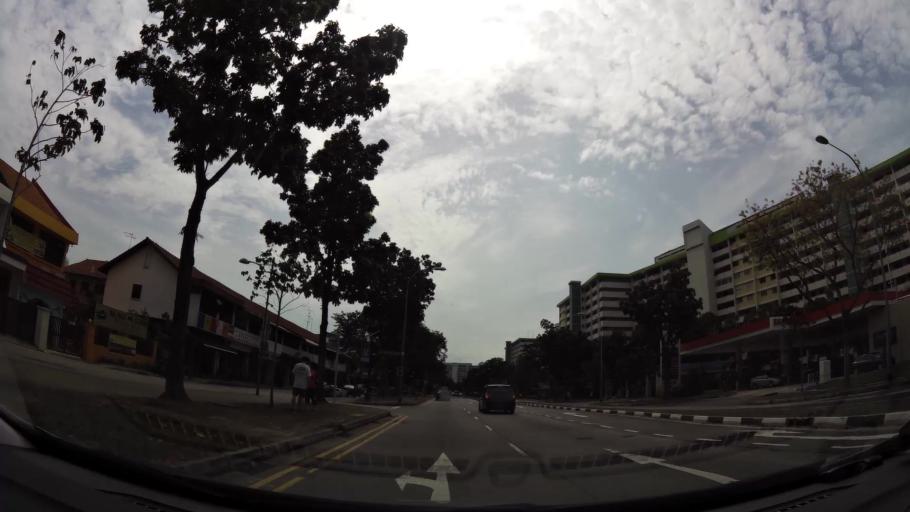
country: SG
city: Singapore
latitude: 1.3086
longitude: 103.7611
